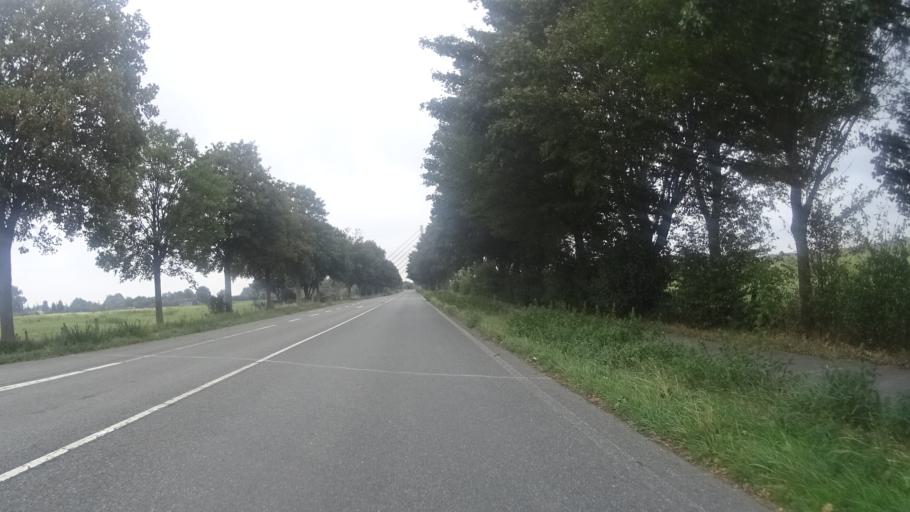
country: DE
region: North Rhine-Westphalia
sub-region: Regierungsbezirk Dusseldorf
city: Wesel
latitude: 51.6380
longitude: 6.5924
